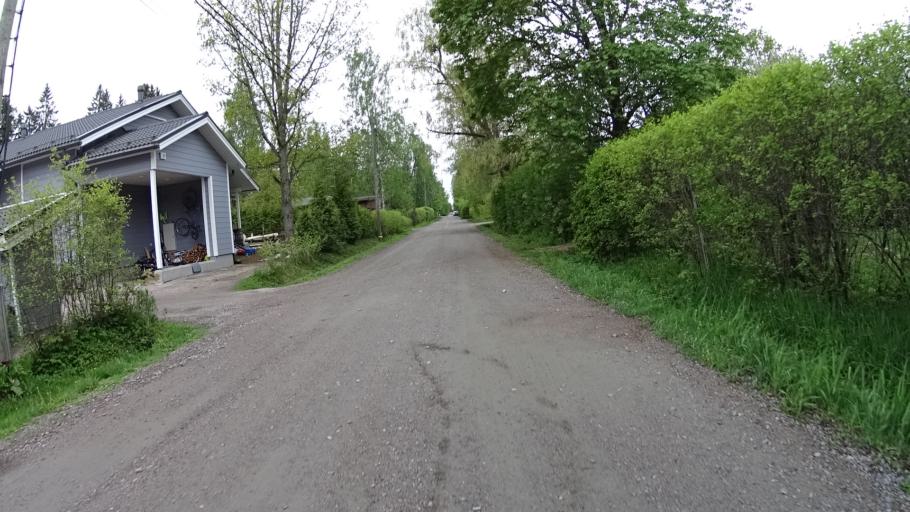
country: FI
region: Uusimaa
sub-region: Helsinki
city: Kauniainen
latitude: 60.2387
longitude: 24.7506
